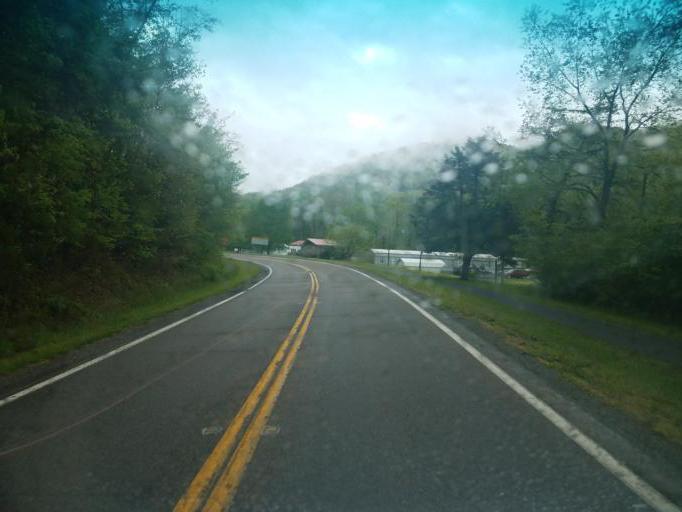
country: US
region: Tennessee
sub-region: Johnson County
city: Mountain City
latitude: 36.6279
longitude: -81.7761
